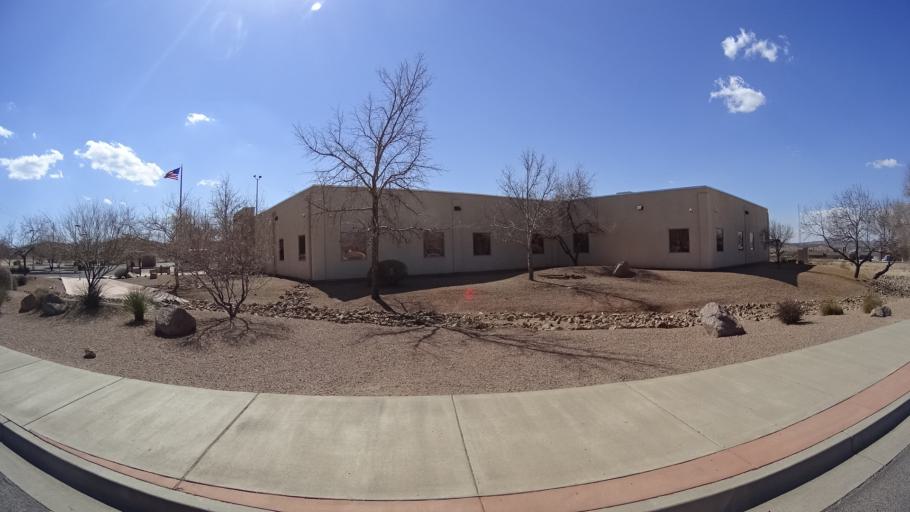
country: US
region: Arizona
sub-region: Mohave County
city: Kingman
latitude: 35.1903
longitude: -114.0144
